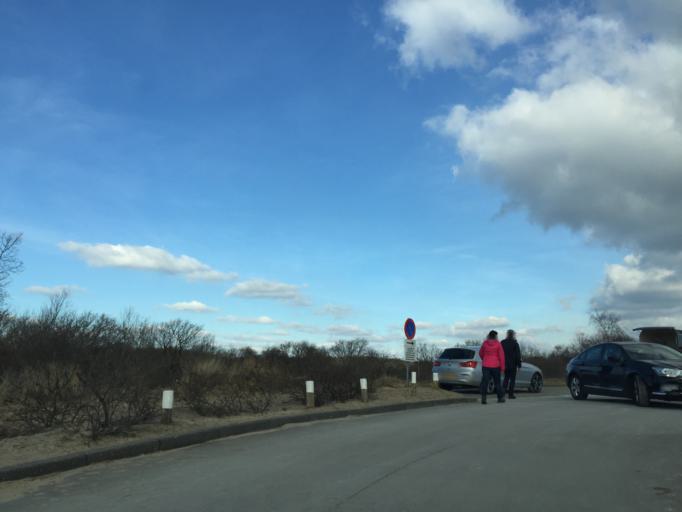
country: NL
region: South Holland
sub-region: Gemeente Wassenaar
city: Wassenaar
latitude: 52.1316
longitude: 4.3528
